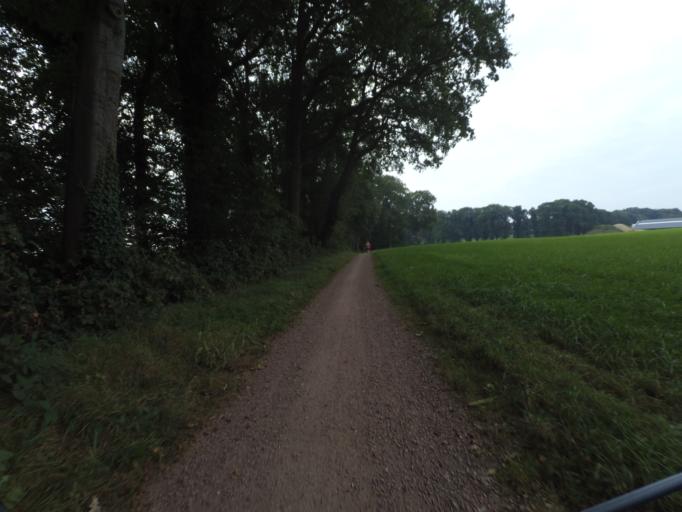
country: NL
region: Overijssel
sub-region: Gemeente Oldenzaal
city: Oldenzaal
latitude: 52.3283
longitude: 6.9798
